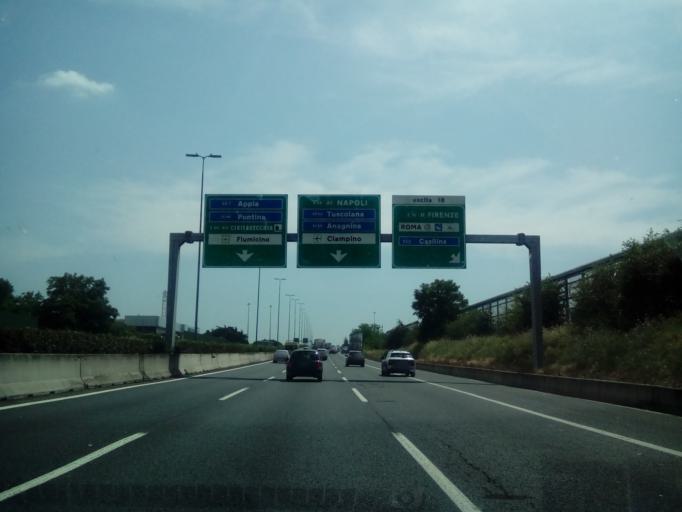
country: IT
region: Latium
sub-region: Citta metropolitana di Roma Capitale
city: Ciampino
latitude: 41.8691
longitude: 12.6036
